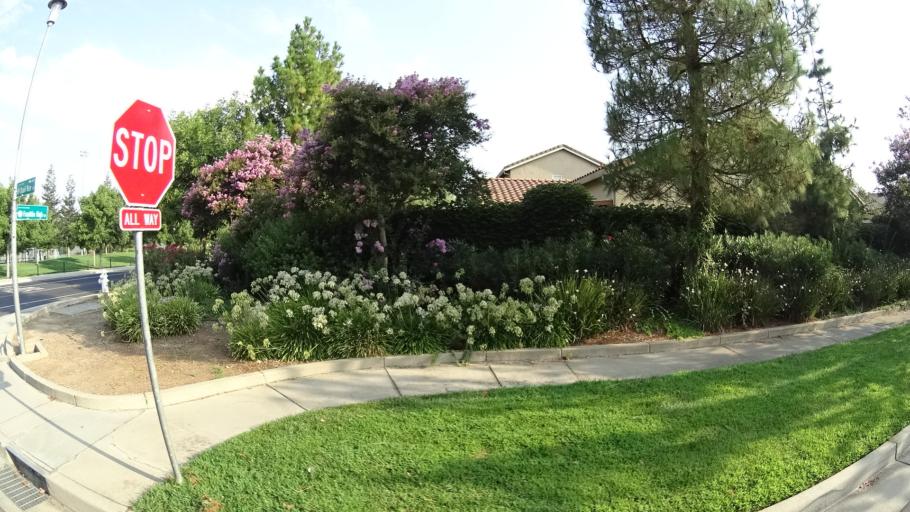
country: US
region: California
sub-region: Sacramento County
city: Laguna
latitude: 38.3905
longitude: -121.4219
